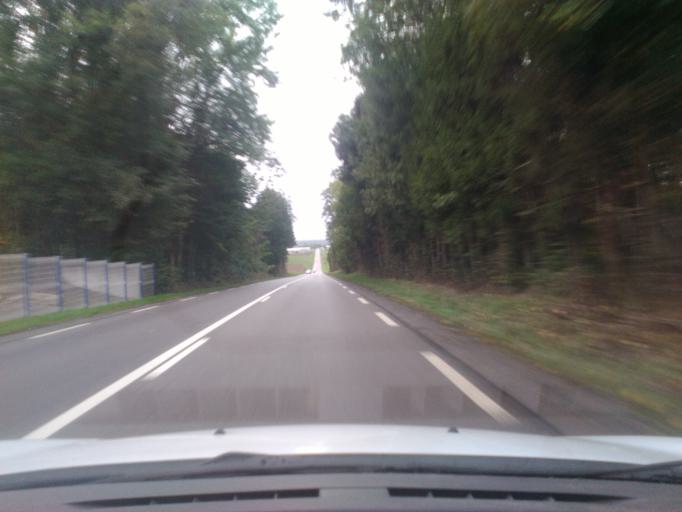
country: FR
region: Lorraine
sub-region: Departement des Vosges
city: Jeanmenil
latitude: 48.3372
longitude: 6.6795
